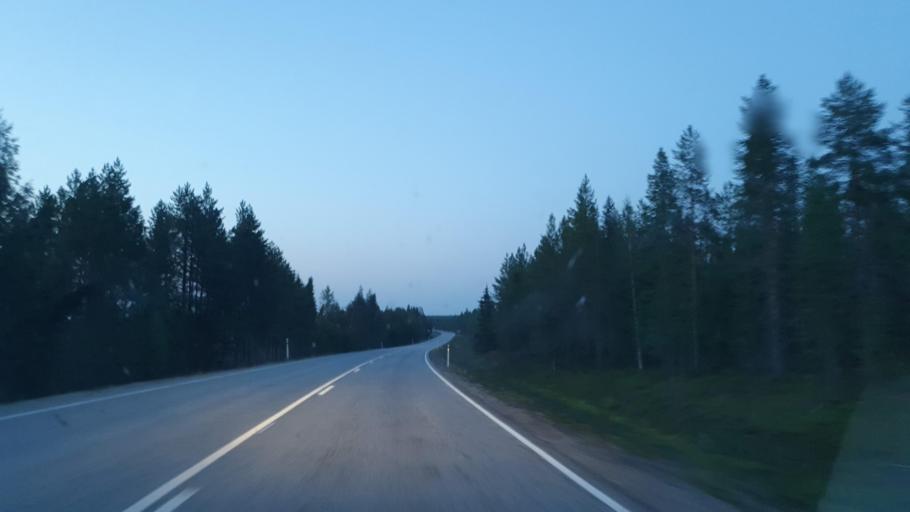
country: FI
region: Northern Ostrobothnia
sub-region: Koillismaa
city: Kuusamo
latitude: 65.6063
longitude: 28.9818
